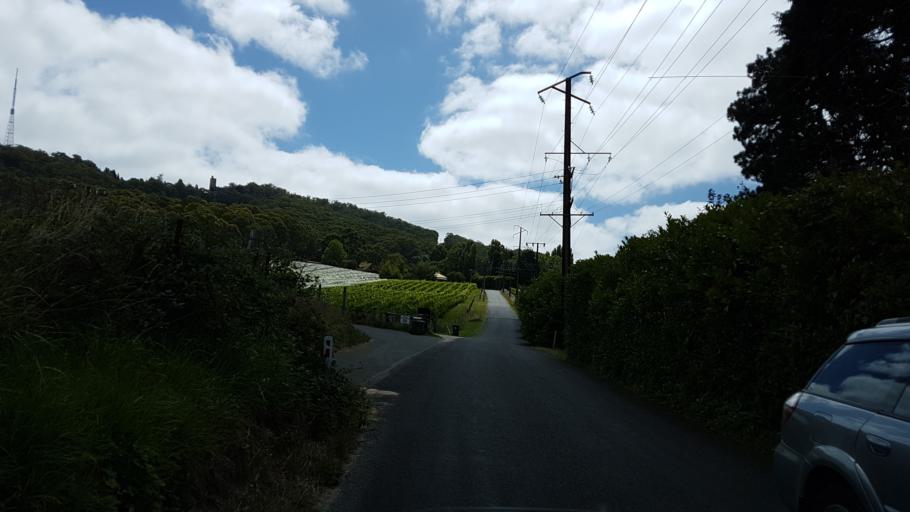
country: AU
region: South Australia
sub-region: Adelaide Hills
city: Crafers
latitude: -34.9815
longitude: 138.7206
